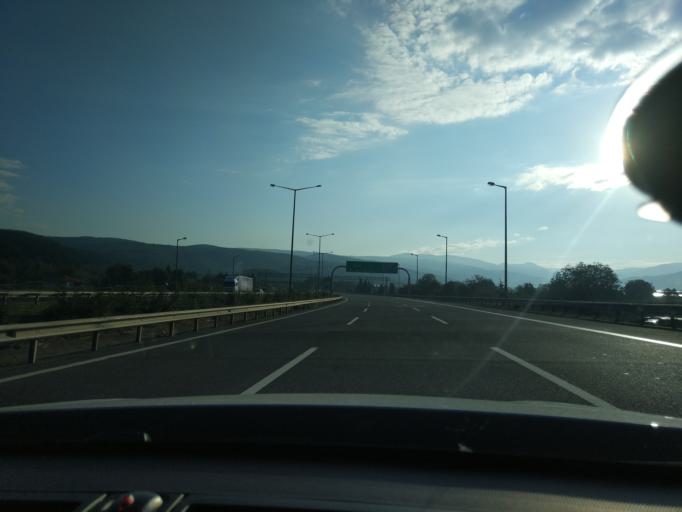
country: TR
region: Duzce
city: Kaynasli
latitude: 40.7853
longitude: 31.2694
